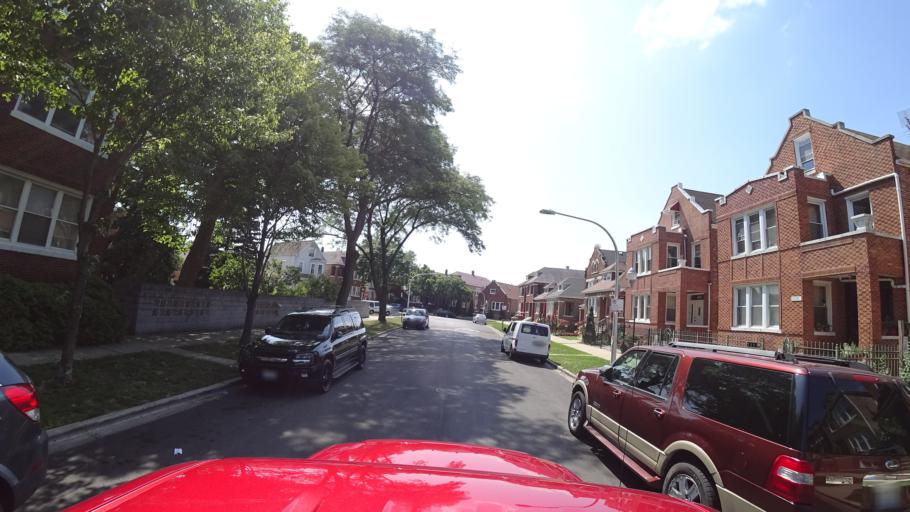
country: US
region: Illinois
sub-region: Cook County
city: Chicago
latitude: 41.8201
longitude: -87.6913
